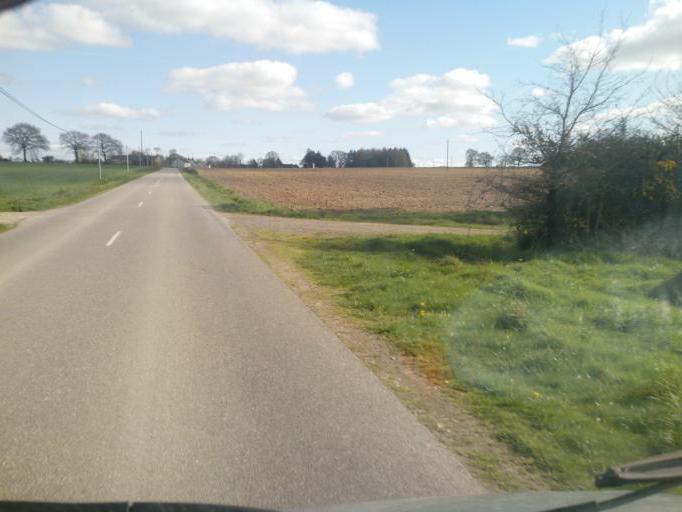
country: FR
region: Brittany
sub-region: Departement d'Ille-et-Vilaine
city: Maxent
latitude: 47.9701
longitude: -2.0190
